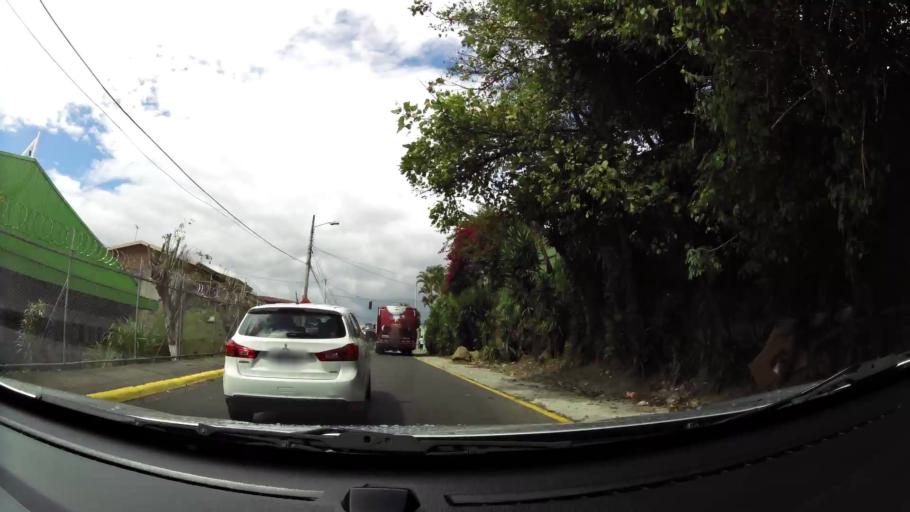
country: CR
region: Cartago
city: Tres Rios
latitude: 9.9087
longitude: -83.9842
